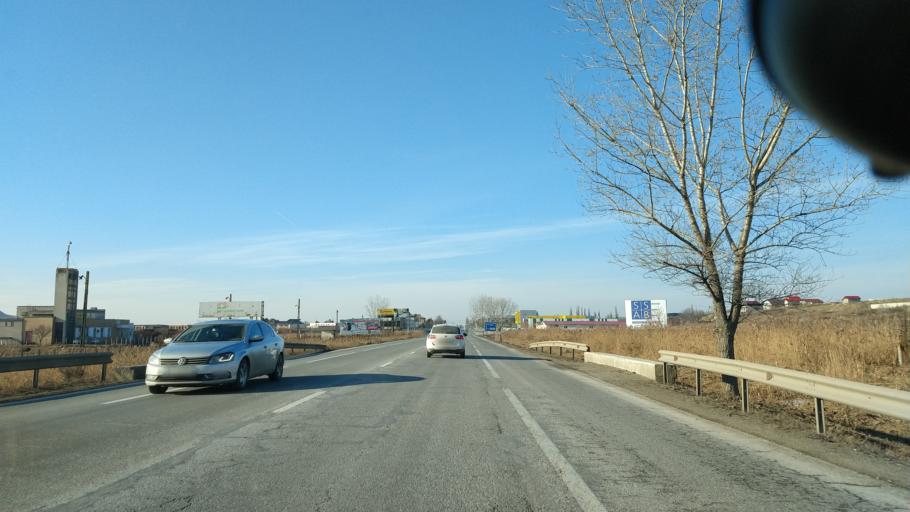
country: RO
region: Iasi
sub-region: Comuna Valea Lupului
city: Valea Lupului
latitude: 47.1839
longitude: 27.4592
